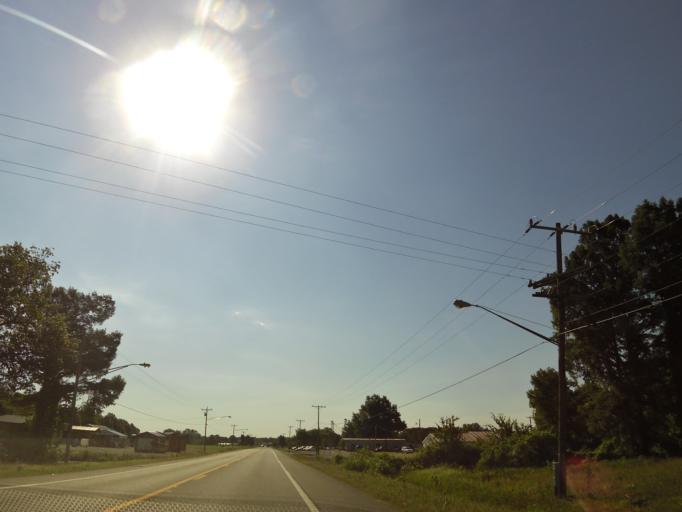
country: US
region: Arkansas
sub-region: Clay County
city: Corning
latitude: 36.4054
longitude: -90.5692
